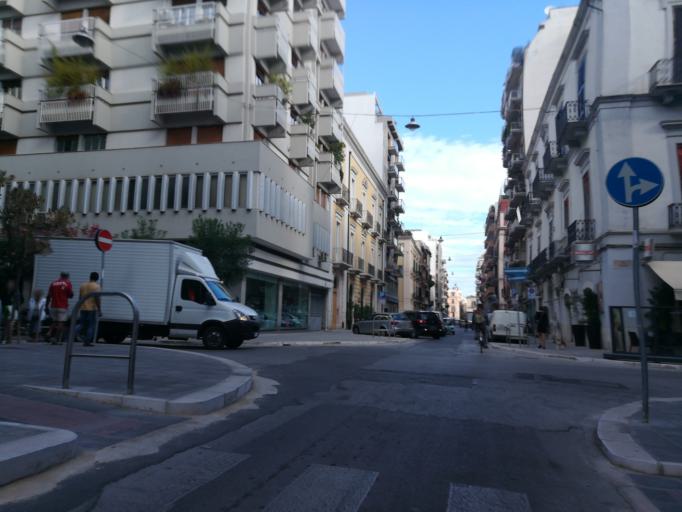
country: IT
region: Apulia
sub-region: Provincia di Bari
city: Bari
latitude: 41.1232
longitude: 16.8714
